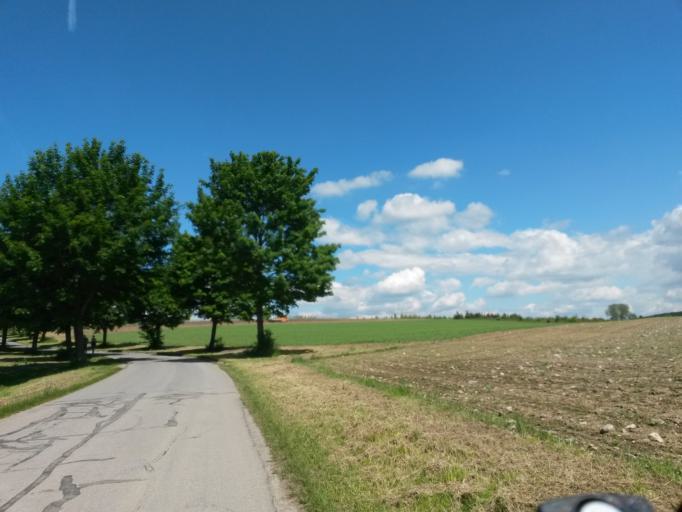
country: DE
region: Baden-Wuerttemberg
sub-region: Tuebingen Region
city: Bad Waldsee
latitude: 47.9306
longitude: 9.7443
